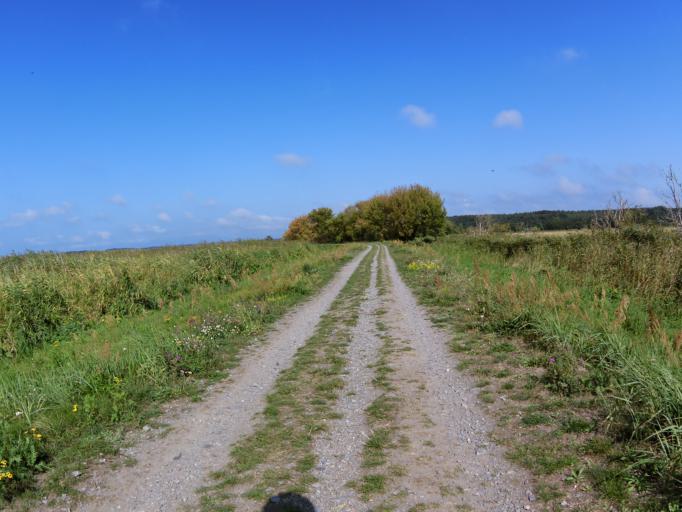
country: DE
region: Mecklenburg-Vorpommern
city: Loddin
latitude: 53.9916
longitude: 14.0479
